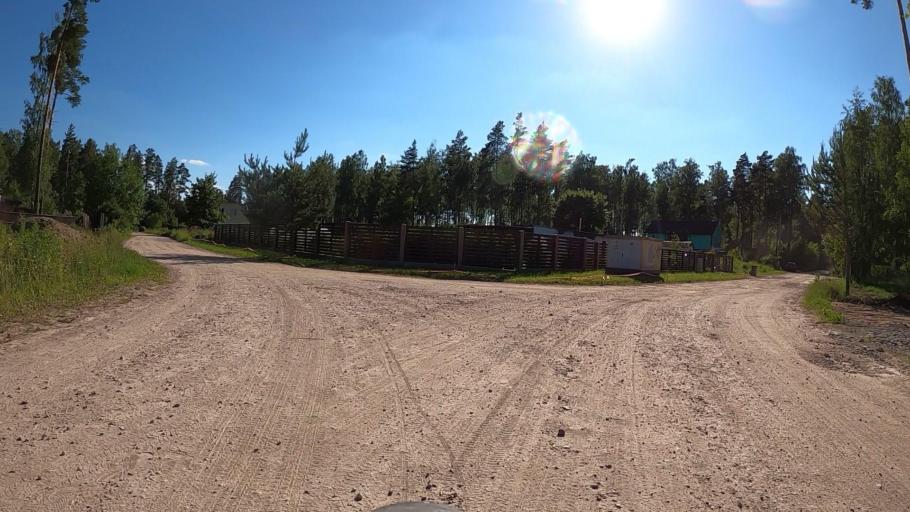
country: LV
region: Stopini
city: Ulbroka
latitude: 56.8751
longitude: 24.2807
